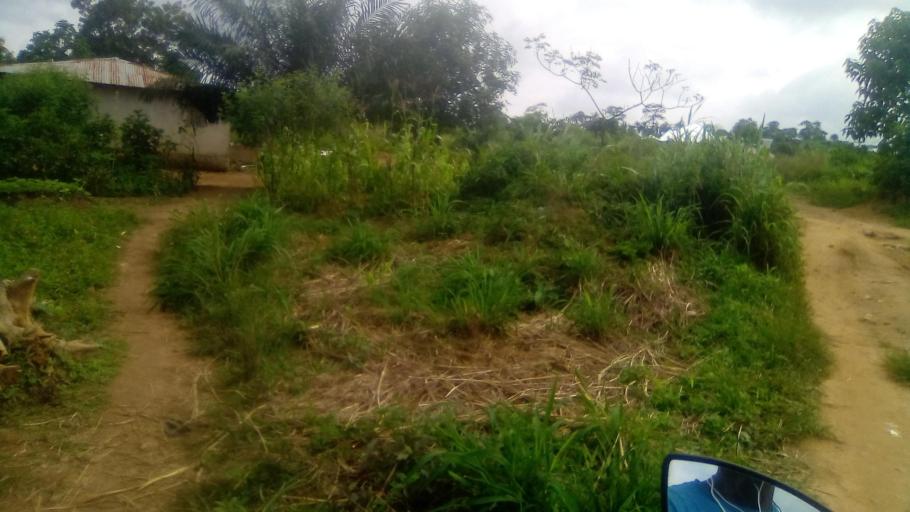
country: SL
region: Eastern Province
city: Kailahun
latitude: 8.2821
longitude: -10.5612
